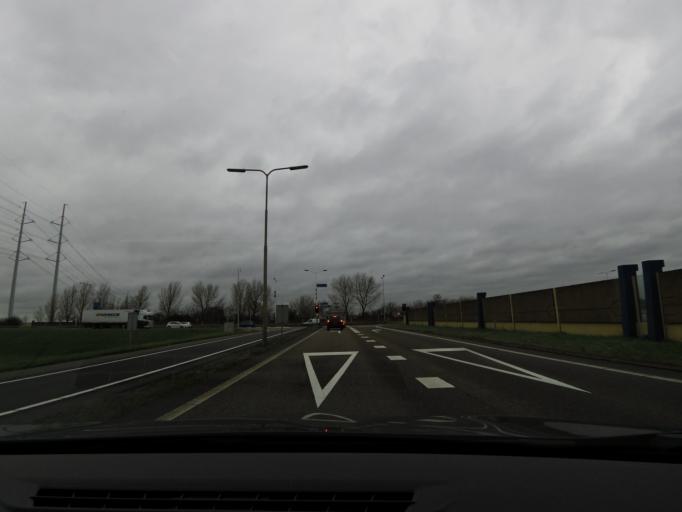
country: NL
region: South Holland
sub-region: Gemeente Delft
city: Delft
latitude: 51.9955
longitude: 4.3197
